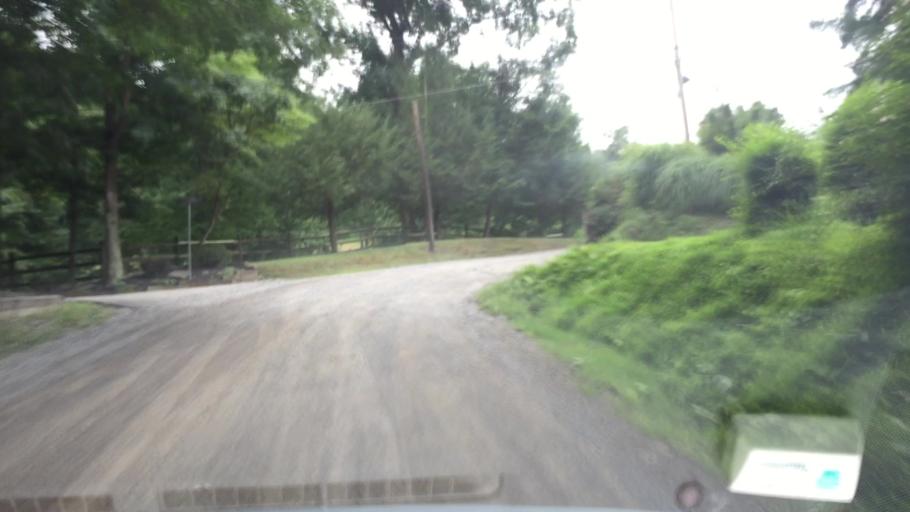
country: US
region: Pennsylvania
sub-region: Allegheny County
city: Allison Park
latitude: 40.5789
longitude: -79.9123
